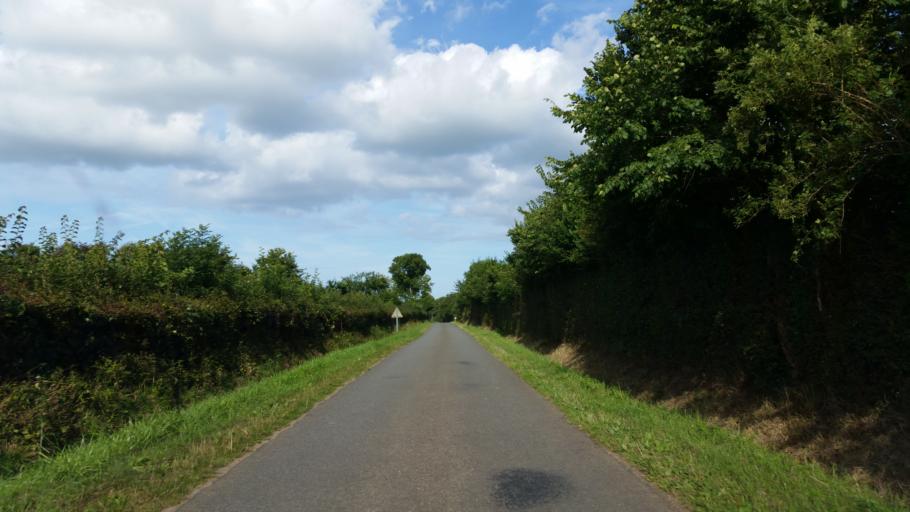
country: FR
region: Lower Normandy
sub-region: Departement de la Manche
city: Sainte-Mere-Eglise
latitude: 49.4524
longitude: -1.2902
